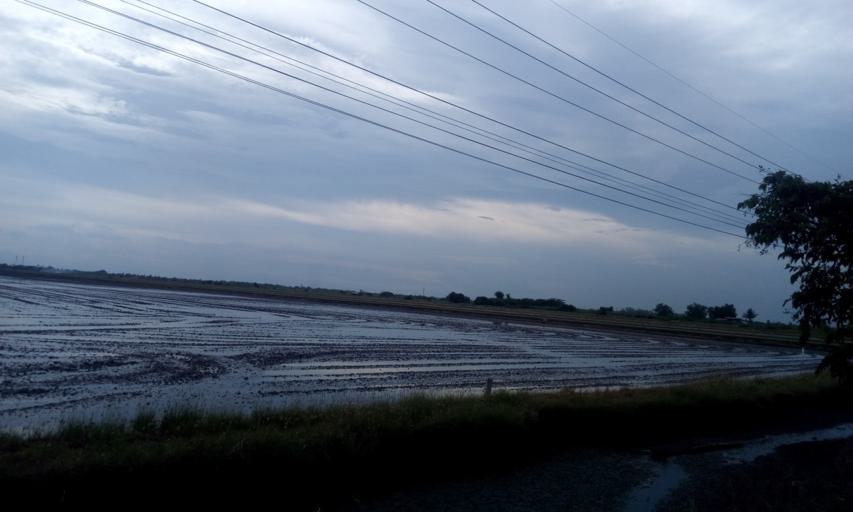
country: TH
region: Pathum Thani
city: Ban Lam Luk Ka
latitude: 14.0220
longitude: 100.8435
